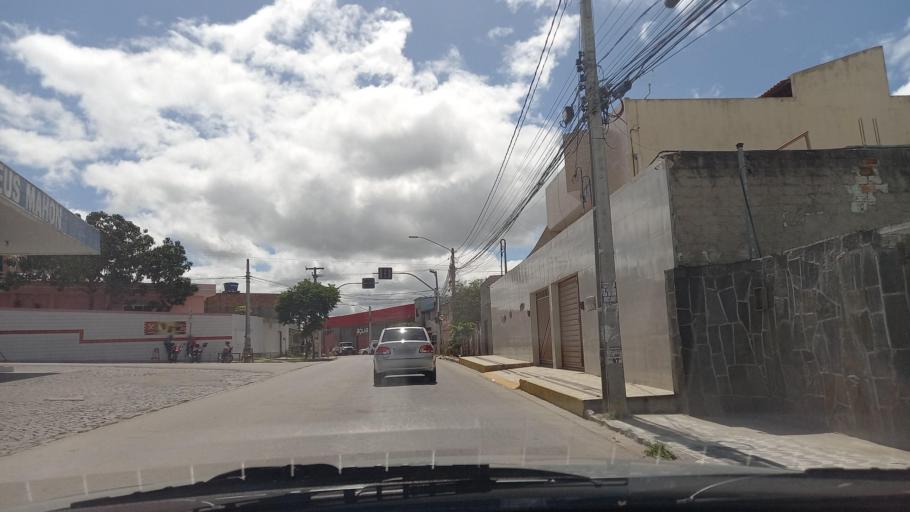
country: BR
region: Pernambuco
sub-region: Caruaru
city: Caruaru
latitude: -8.2701
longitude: -35.9619
